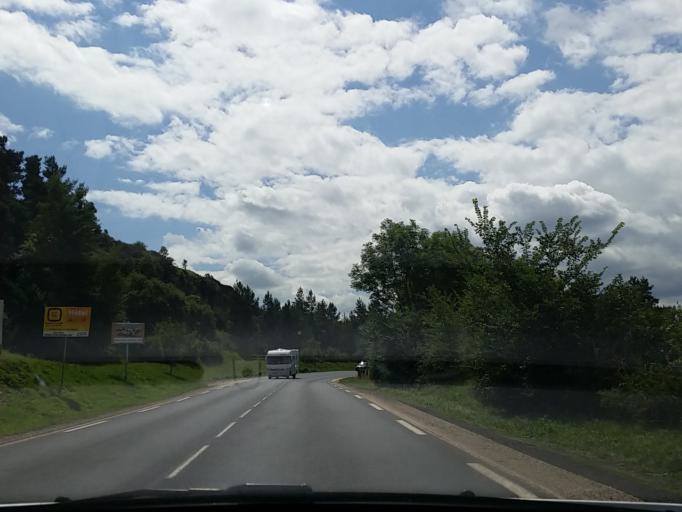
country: FR
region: Auvergne
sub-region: Departement du Cantal
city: Saint-Flour
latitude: 45.0444
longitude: 3.1081
